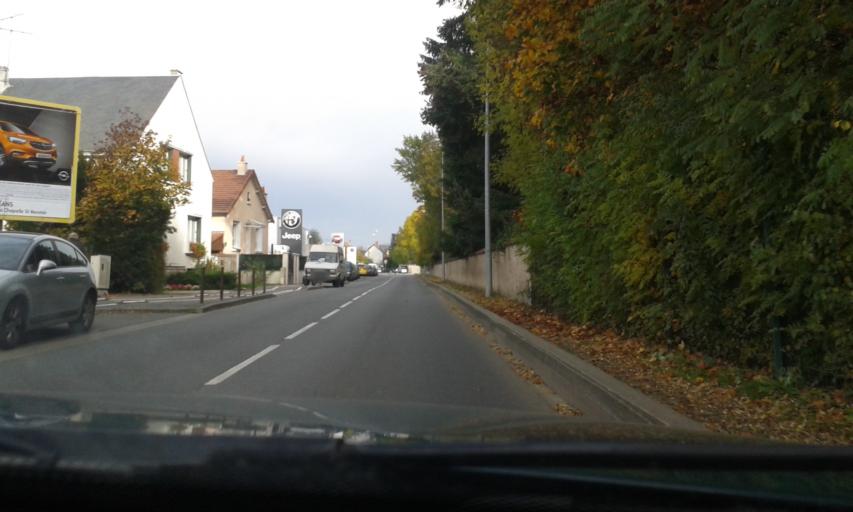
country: FR
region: Centre
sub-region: Departement du Loiret
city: Saint-Jean-le-Blanc
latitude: 47.8746
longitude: 1.9137
